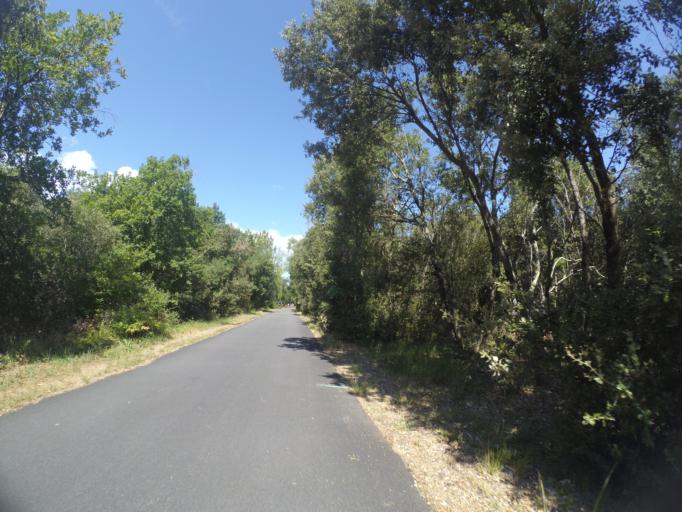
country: FR
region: Poitou-Charentes
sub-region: Departement de la Charente-Maritime
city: Les Mathes
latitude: 45.6779
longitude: -1.1541
